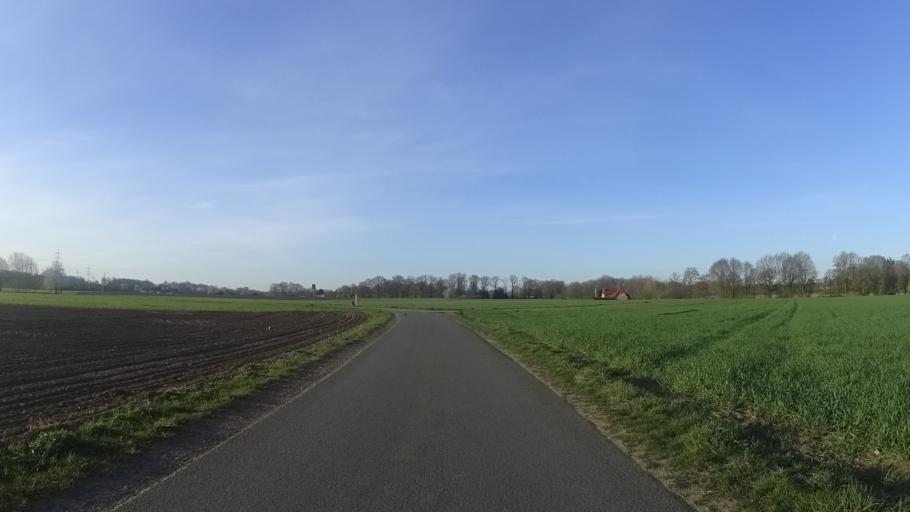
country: DE
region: North Rhine-Westphalia
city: Emsdetten
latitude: 52.1967
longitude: 7.5264
